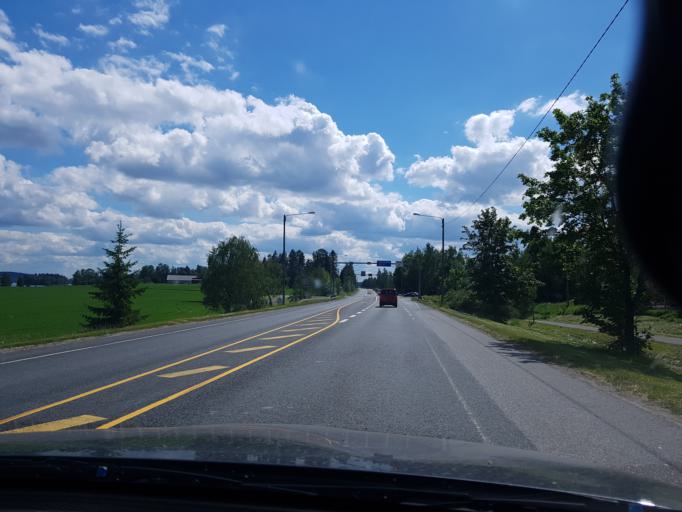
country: FI
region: Haeme
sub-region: Haemeenlinna
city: Parola
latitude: 61.0614
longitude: 24.3922
